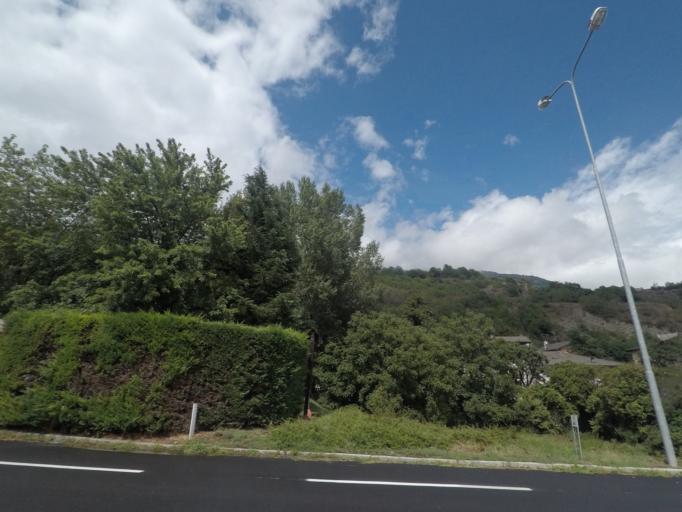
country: IT
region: Aosta Valley
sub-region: Valle d'Aosta
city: Quart
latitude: 45.7407
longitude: 7.4124
